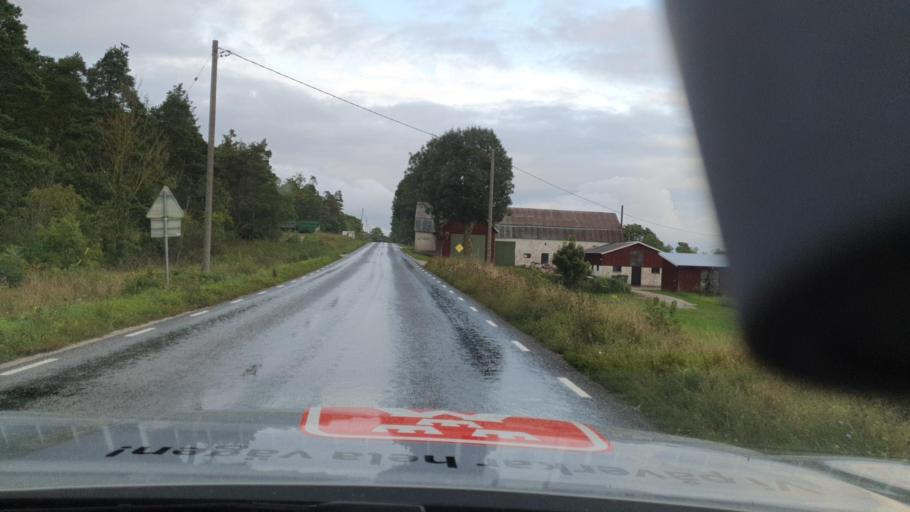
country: SE
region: Gotland
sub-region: Gotland
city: Vibble
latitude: 57.5351
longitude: 18.2537
